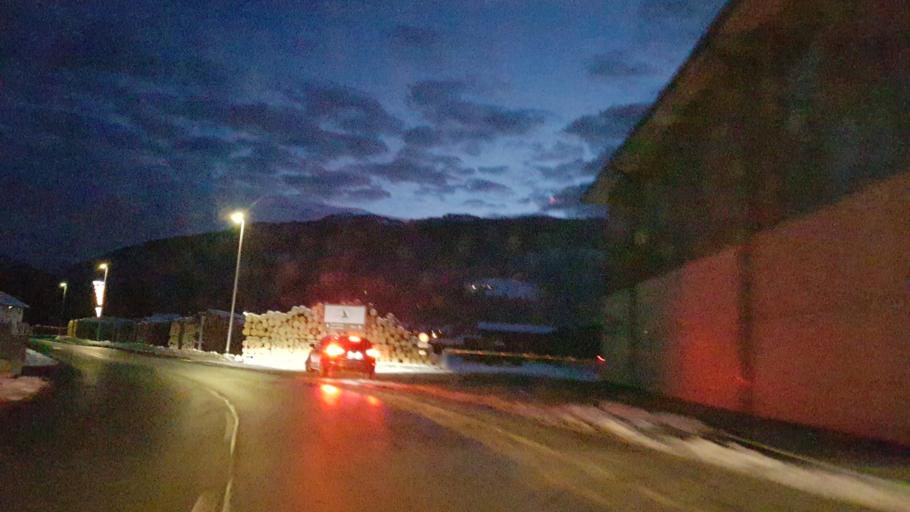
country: AT
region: Salzburg
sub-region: Politischer Bezirk Sankt Johann im Pongau
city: Radstadt
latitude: 47.3822
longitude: 13.4731
